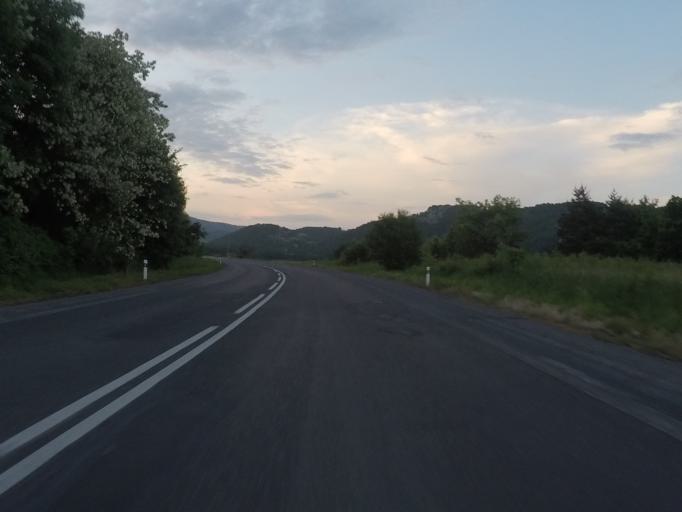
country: SK
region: Banskobystricky
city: Rimavska Sobota
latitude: 48.4834
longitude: 19.9451
